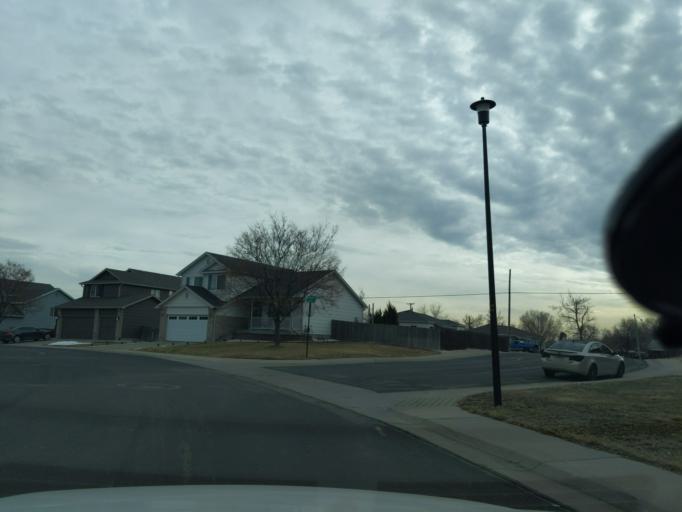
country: US
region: Colorado
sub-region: Adams County
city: Thornton
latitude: 39.8675
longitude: -104.9520
